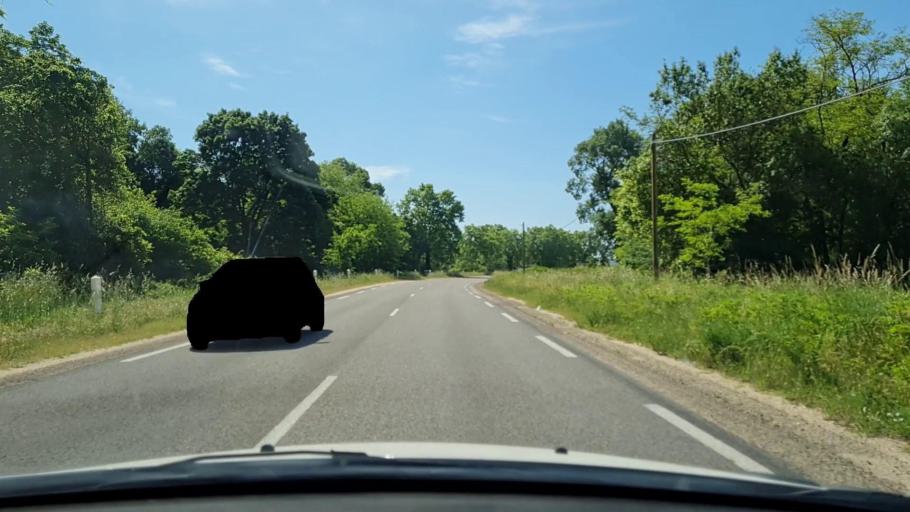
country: FR
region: Languedoc-Roussillon
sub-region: Departement du Gard
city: Saint-Genies-de-Malgoires
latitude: 43.9543
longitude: 4.2451
